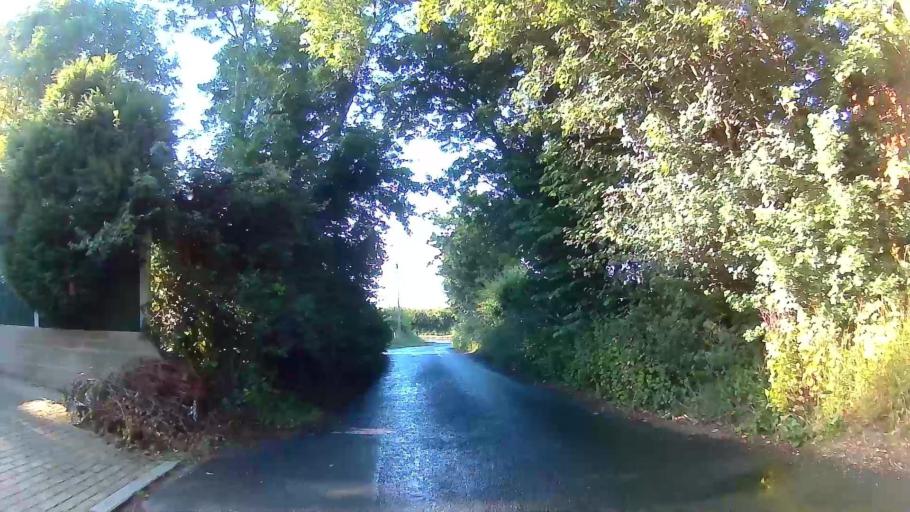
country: GB
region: England
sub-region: Essex
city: Writtle
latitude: 51.7403
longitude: 0.4404
